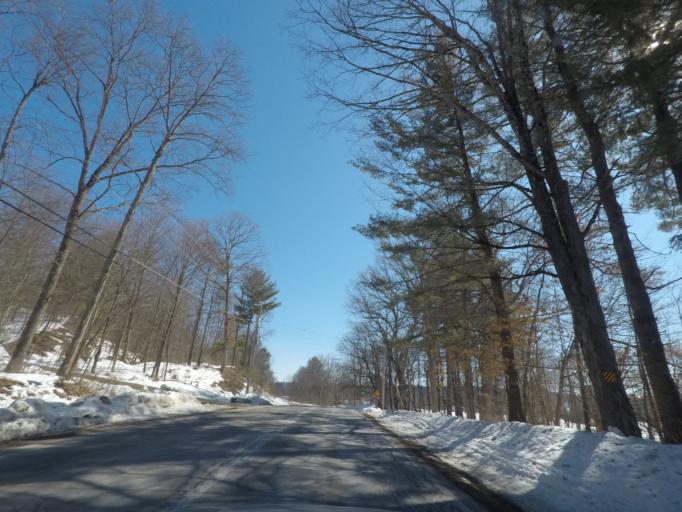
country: US
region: New York
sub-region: Saratoga County
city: Schuylerville
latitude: 43.1212
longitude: -73.5756
